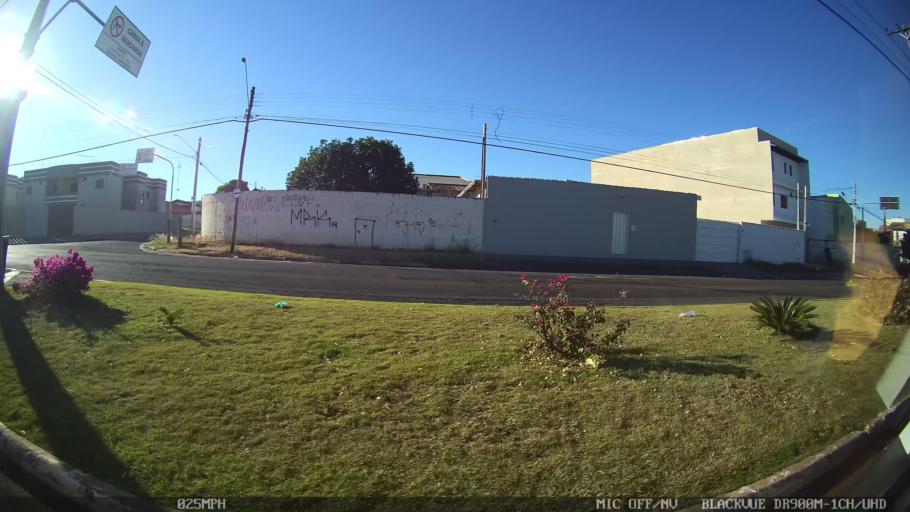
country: BR
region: Sao Paulo
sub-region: Franca
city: Franca
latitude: -20.5708
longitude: -47.4066
